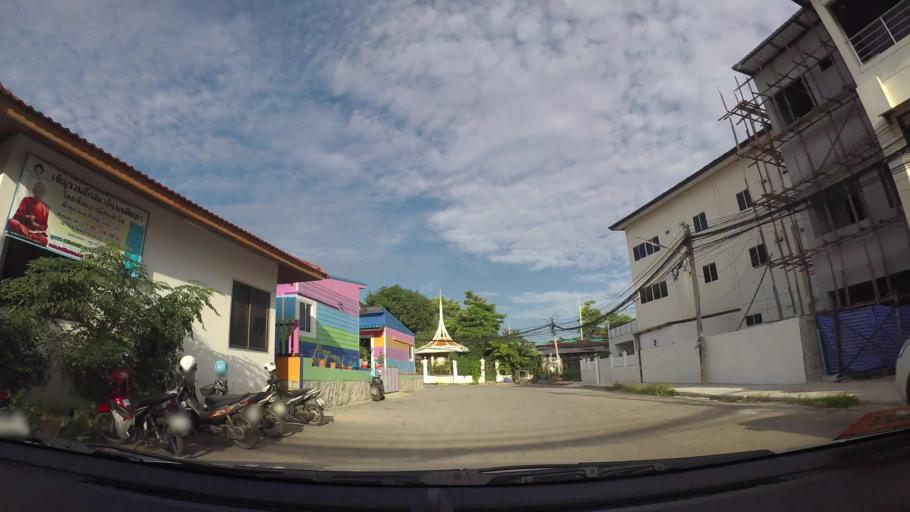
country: TH
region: Chon Buri
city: Sattahip
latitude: 12.6676
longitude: 100.9211
